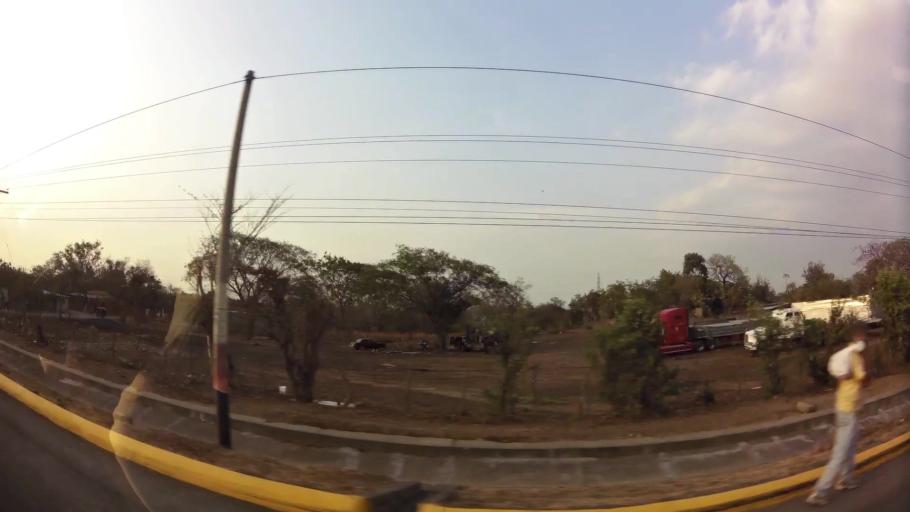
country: NI
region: Leon
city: Nagarote
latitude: 12.2728
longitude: -86.5652
